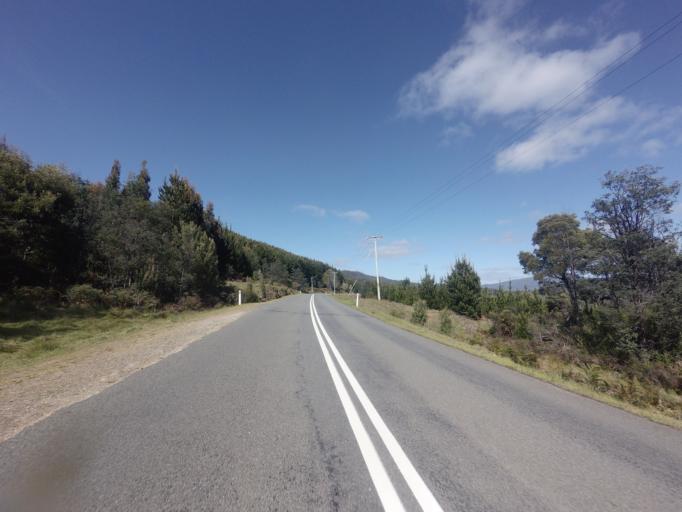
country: AU
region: Tasmania
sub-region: Derwent Valley
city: New Norfolk
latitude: -42.7428
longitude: 146.6570
